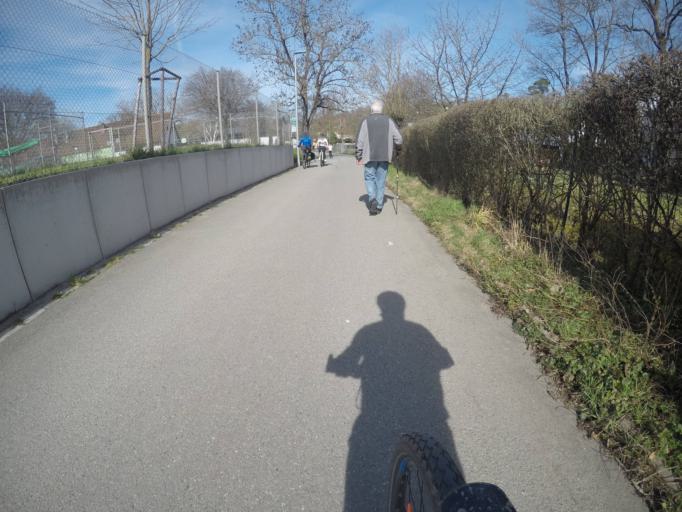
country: DE
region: Baden-Wuerttemberg
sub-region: Regierungsbezirk Stuttgart
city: Korntal
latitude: 48.8131
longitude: 9.1270
